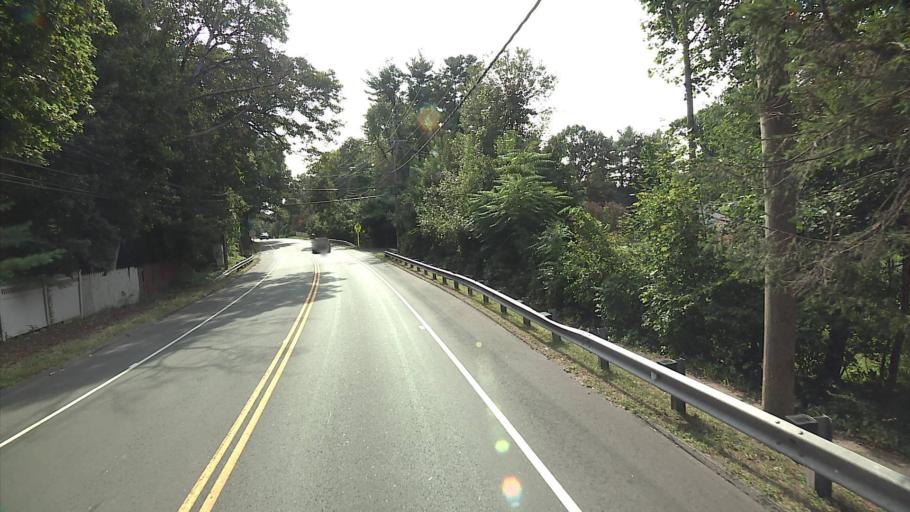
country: US
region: Connecticut
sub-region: Fairfield County
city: Norwalk
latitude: 41.1300
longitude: -73.4419
